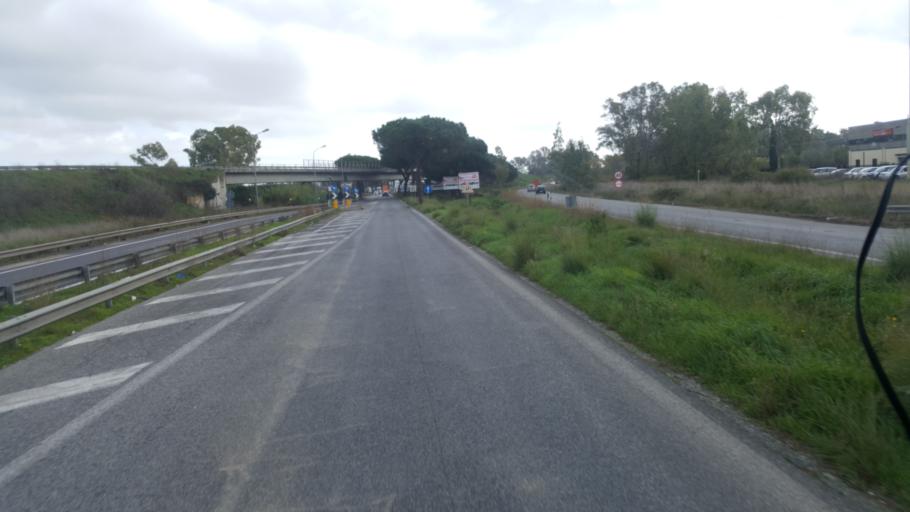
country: IT
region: Latium
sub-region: Provincia di Latina
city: Borgo Podgora
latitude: 41.4843
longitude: 12.8577
